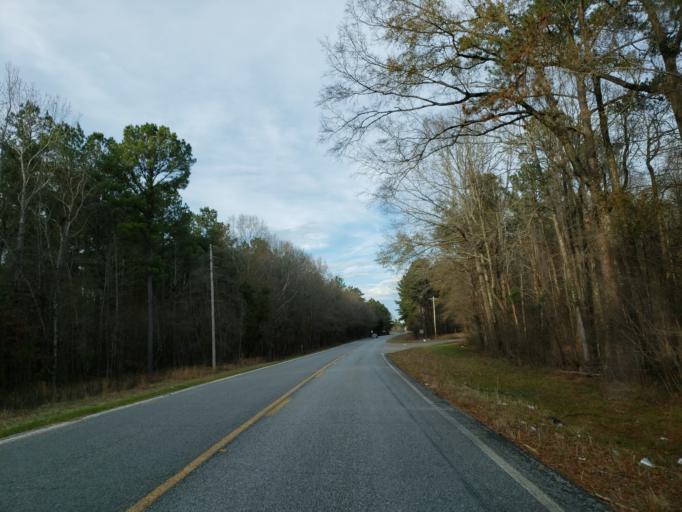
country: US
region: Mississippi
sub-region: Wayne County
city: Waynesboro
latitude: 31.8389
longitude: -88.6883
